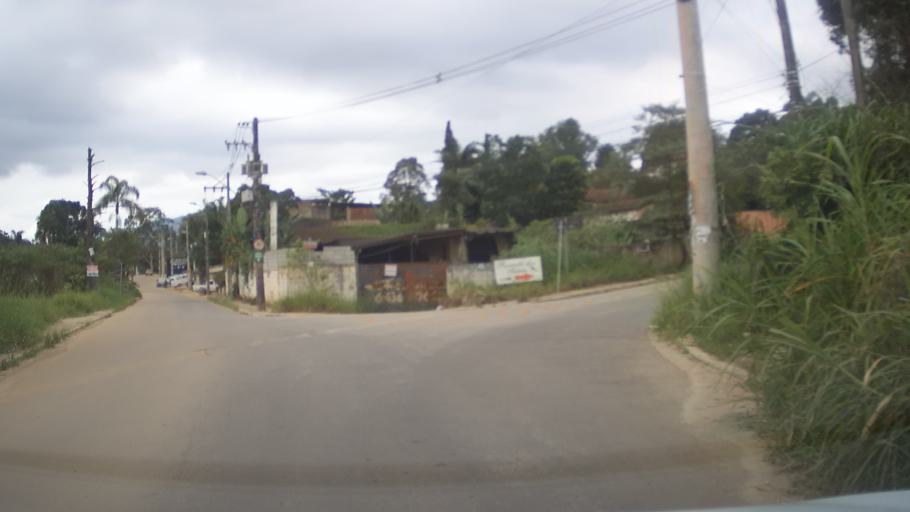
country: BR
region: Sao Paulo
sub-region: Aruja
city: Aruja
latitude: -23.3703
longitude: -46.4012
